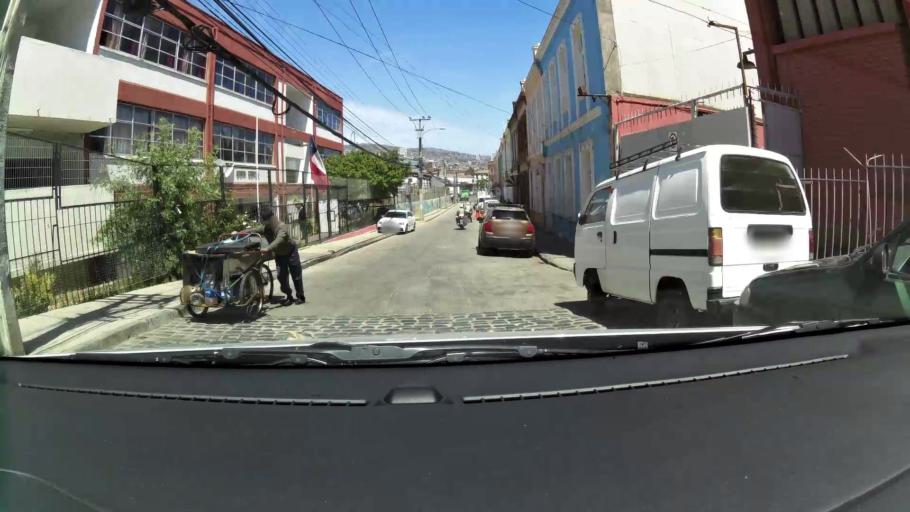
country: CL
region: Valparaiso
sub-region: Provincia de Valparaiso
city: Valparaiso
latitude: -33.0511
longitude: -71.6010
